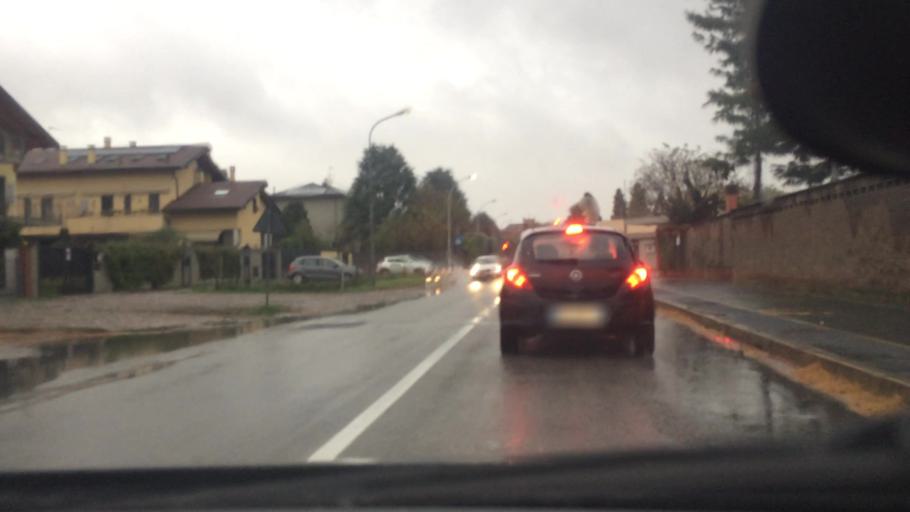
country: IT
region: Lombardy
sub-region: Citta metropolitana di Milano
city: Nerviano
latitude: 45.5454
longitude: 8.9743
